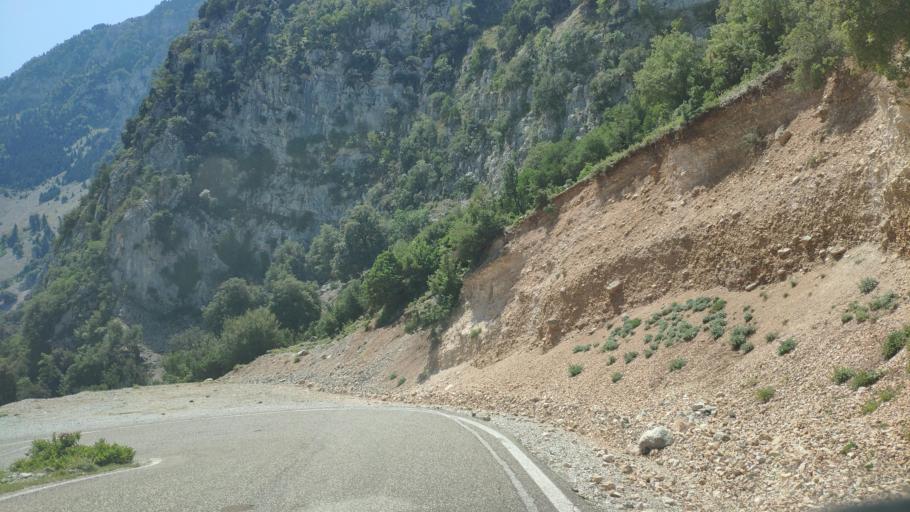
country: GR
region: West Greece
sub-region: Nomos Aitolias kai Akarnanias
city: Krikellos
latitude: 39.0069
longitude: 21.3621
